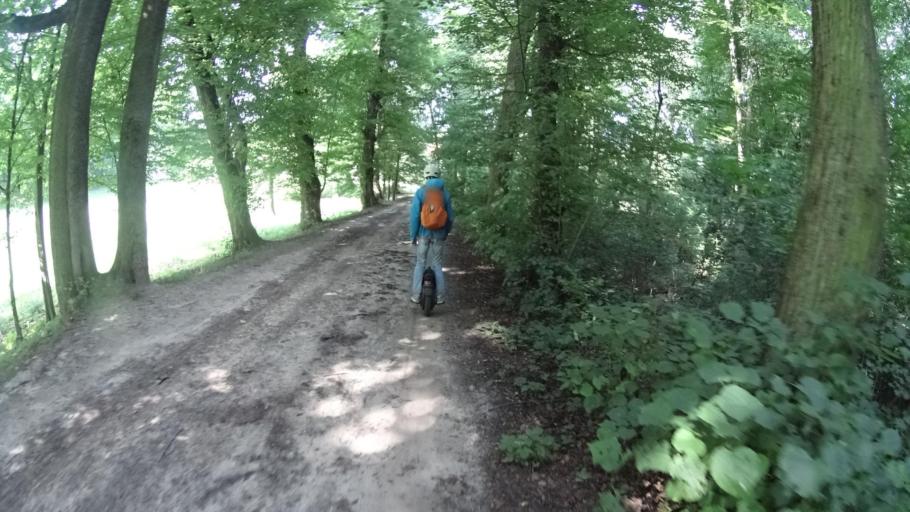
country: PL
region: Masovian Voivodeship
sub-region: Powiat legionowski
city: Jablonna
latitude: 52.3737
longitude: 20.9134
